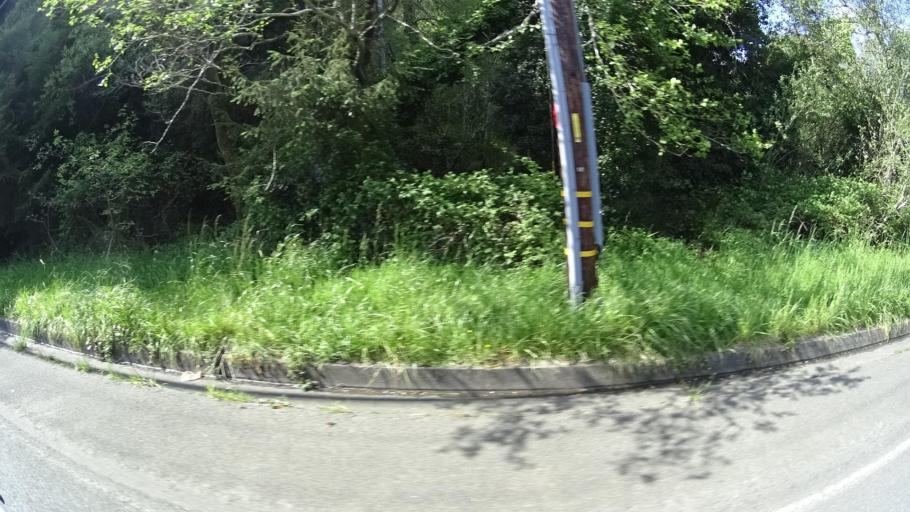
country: US
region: California
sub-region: Humboldt County
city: Cutten
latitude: 40.7677
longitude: -124.1573
